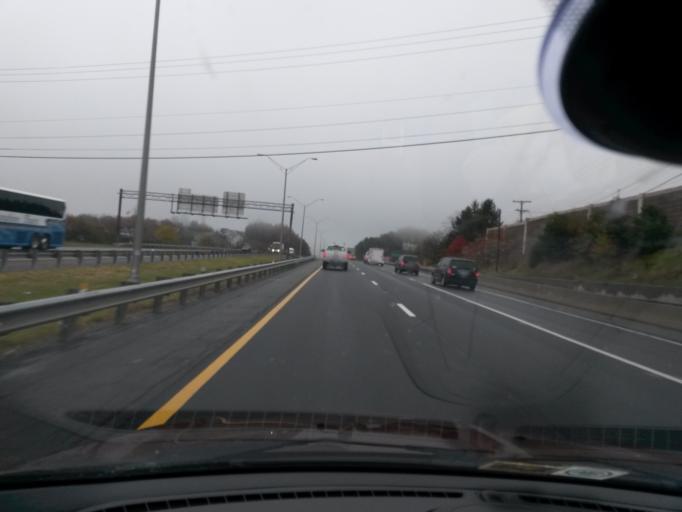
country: US
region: Virginia
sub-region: Montgomery County
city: Christiansburg
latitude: 37.1360
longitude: -80.3772
